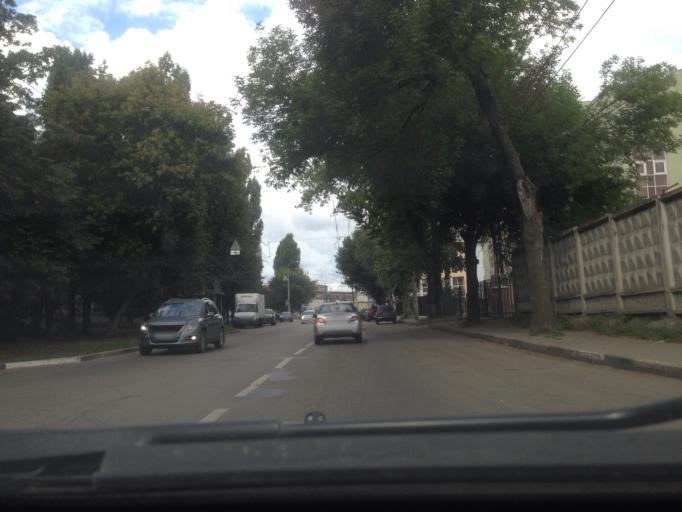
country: RU
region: Voronezj
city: Voronezh
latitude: 51.6730
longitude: 39.1911
